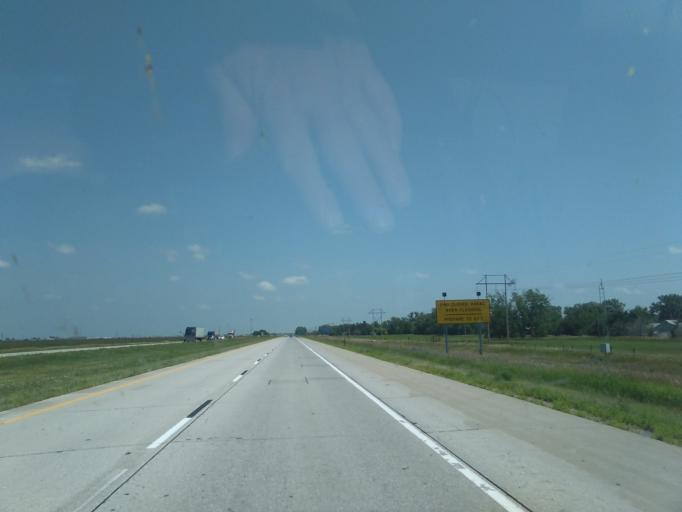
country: US
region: Nebraska
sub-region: Dawson County
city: Lexington
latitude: 40.7484
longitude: -99.7702
